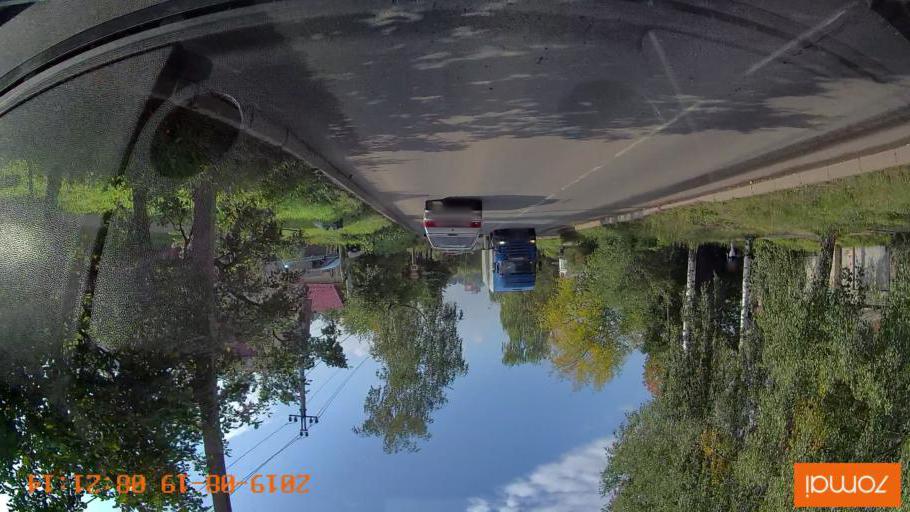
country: RU
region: Ivanovo
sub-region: Gorod Ivanovo
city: Ivanovo
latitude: 56.9808
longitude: 41.0066
